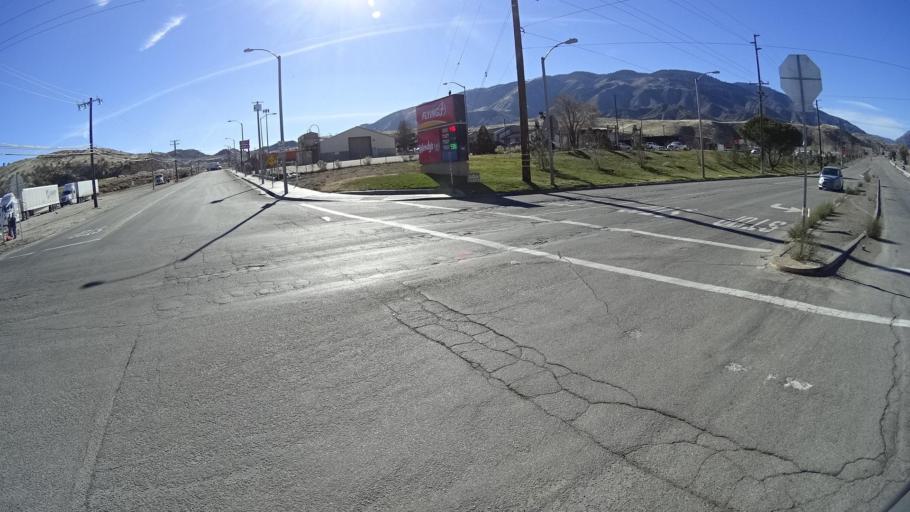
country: US
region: California
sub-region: Kern County
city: Lebec
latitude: 34.8183
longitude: -118.8852
